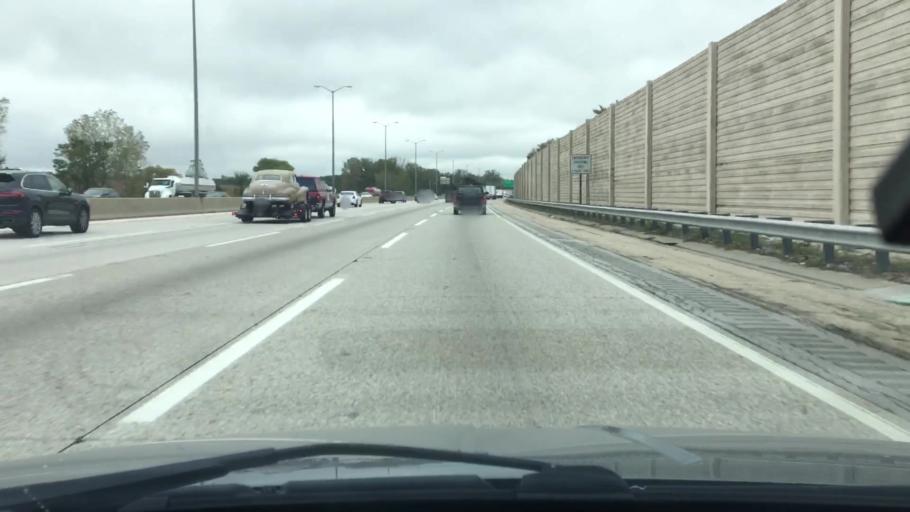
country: US
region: Illinois
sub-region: Lake County
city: Bannockburn
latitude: 42.1875
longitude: -87.8795
